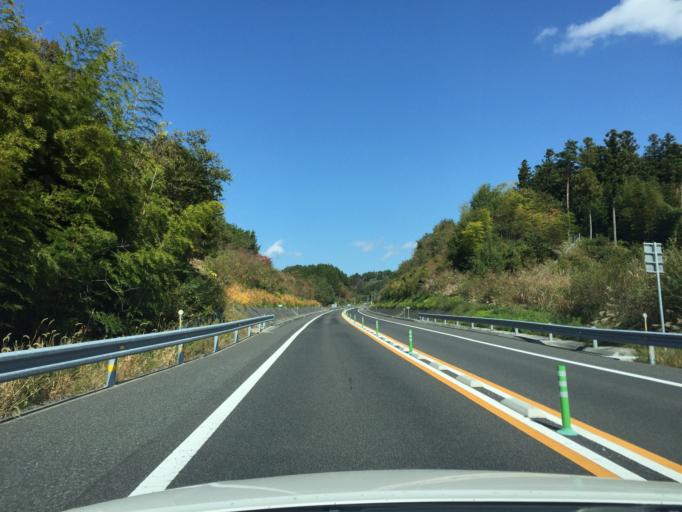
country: JP
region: Fukushima
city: Ishikawa
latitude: 37.2582
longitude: 140.5651
